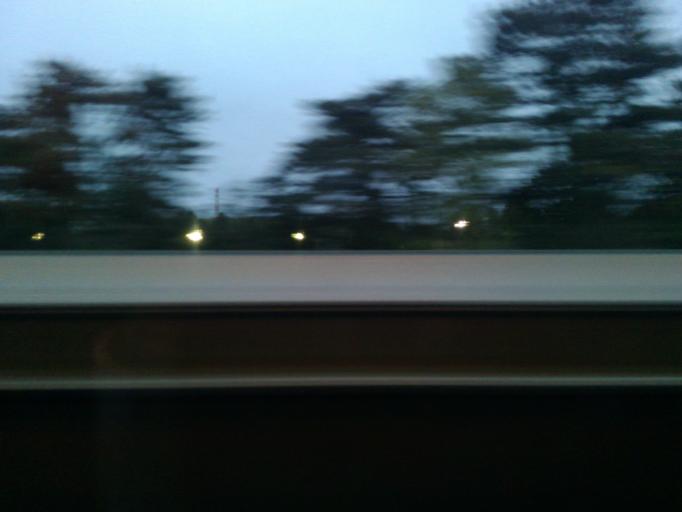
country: JP
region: Tochigi
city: Mibu
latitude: 36.4049
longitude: 139.8597
